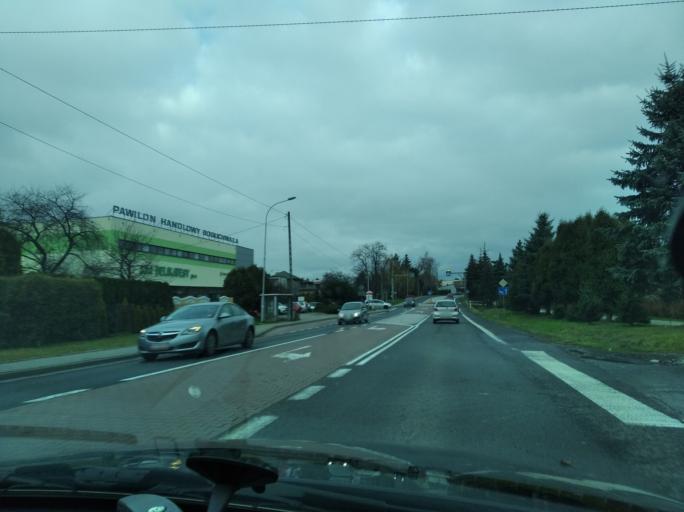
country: PL
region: Subcarpathian Voivodeship
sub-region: Powiat rzeszowski
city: Boguchwala
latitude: 49.9815
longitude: 21.9390
